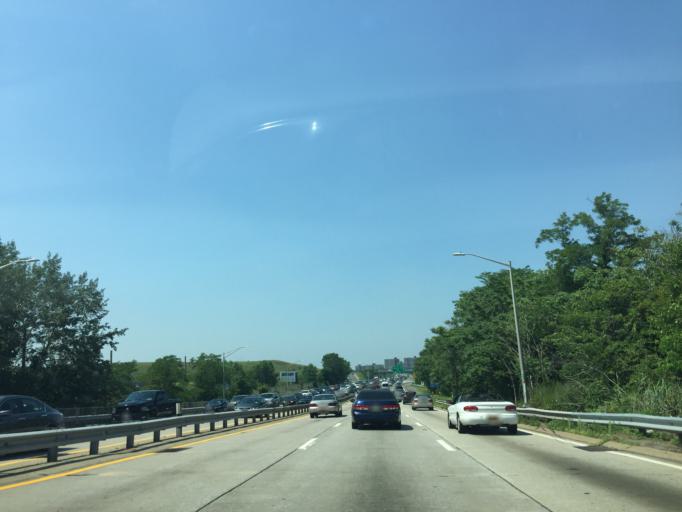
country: US
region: New York
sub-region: Kings County
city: East New York
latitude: 40.6548
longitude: -73.8605
